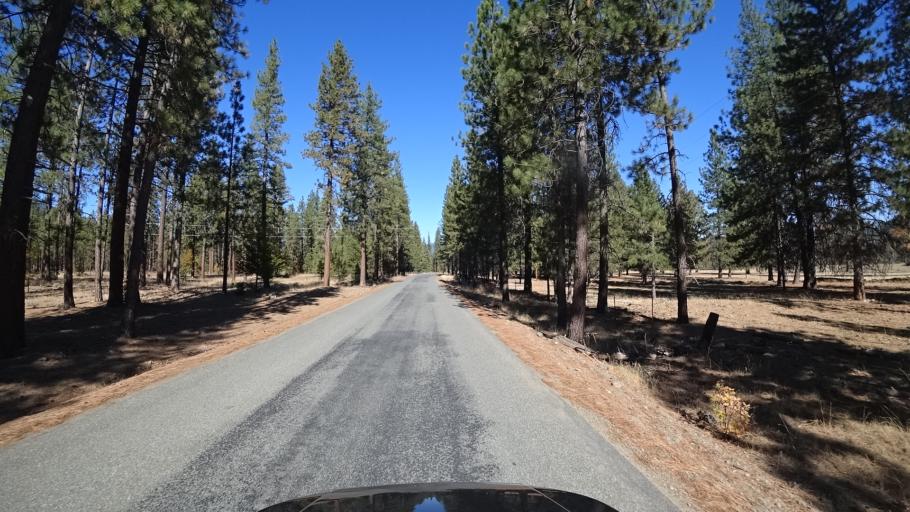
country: US
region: California
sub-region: Siskiyou County
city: Yreka
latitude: 41.5899
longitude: -122.9747
